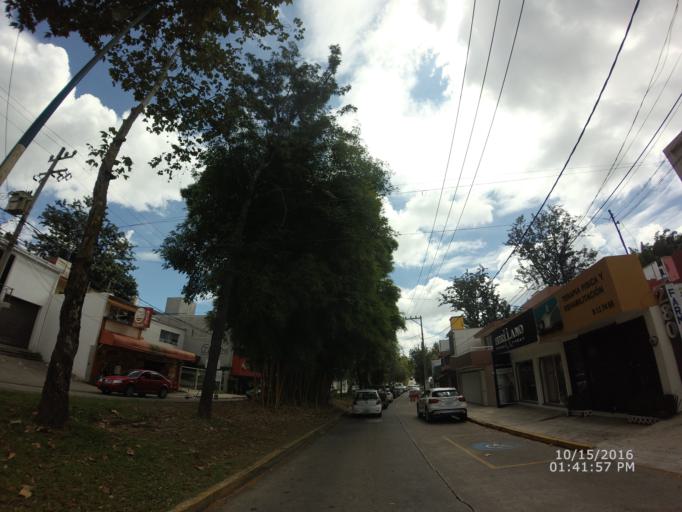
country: MX
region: Veracruz
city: El Castillo
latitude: 19.5329
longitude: -96.8881
